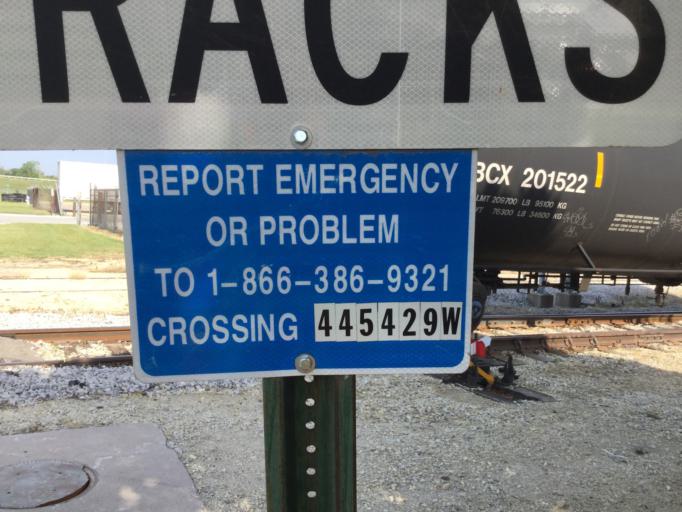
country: US
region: Kansas
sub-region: Harvey County
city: Newton
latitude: 38.0369
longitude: -97.3207
